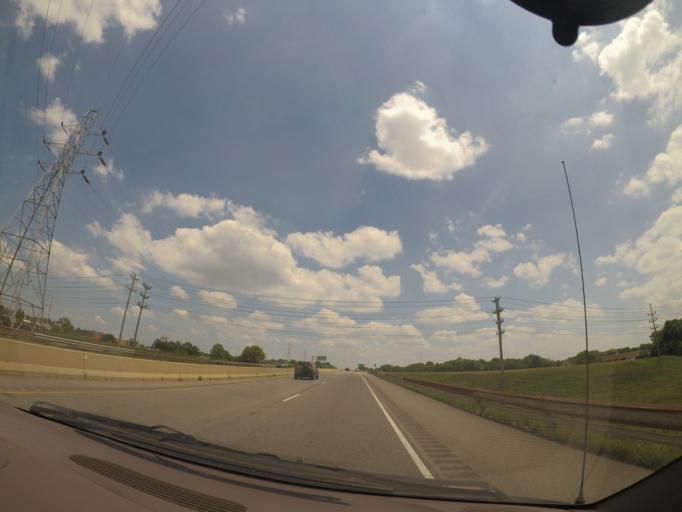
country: US
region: Indiana
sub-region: Saint Joseph County
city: Gulivoire Park
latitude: 41.6244
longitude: -86.2546
